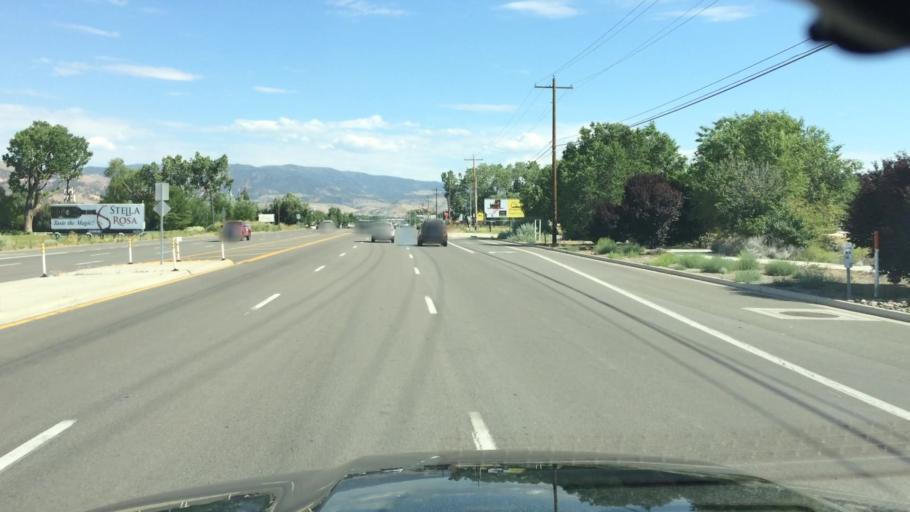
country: US
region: Nevada
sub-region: Washoe County
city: Sparks
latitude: 39.4253
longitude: -119.7608
